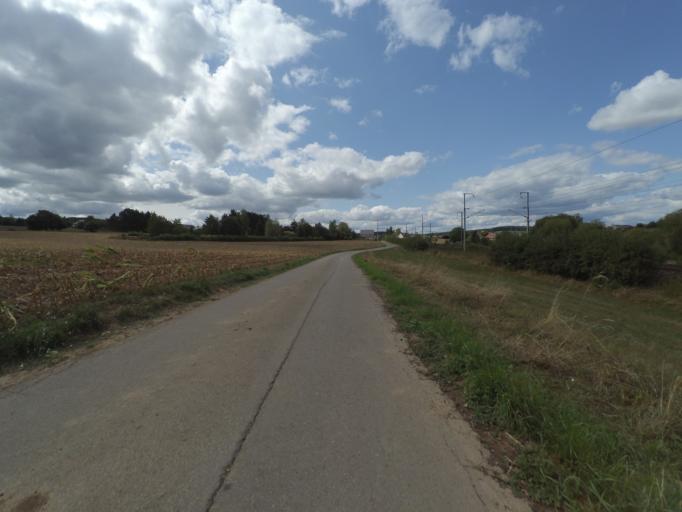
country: LU
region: Grevenmacher
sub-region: Canton de Grevenmacher
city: Betzdorf
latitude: 49.6810
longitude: 6.3227
